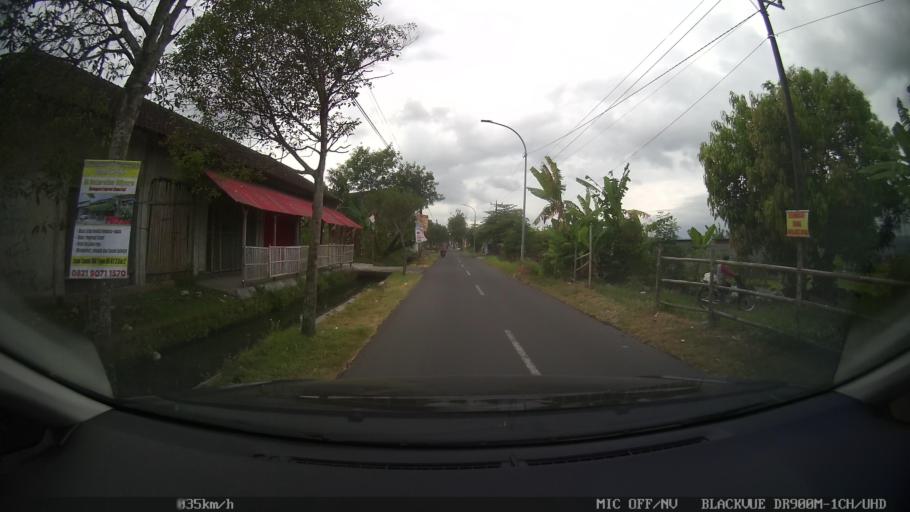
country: ID
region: Daerah Istimewa Yogyakarta
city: Sewon
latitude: -7.8363
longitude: 110.4169
